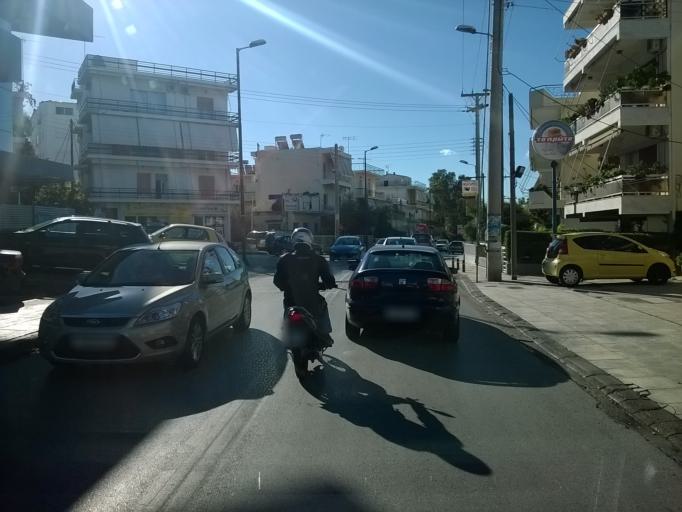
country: GR
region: Attica
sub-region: Nomarchia Athinas
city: Argyroupoli
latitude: 37.8950
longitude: 23.7612
